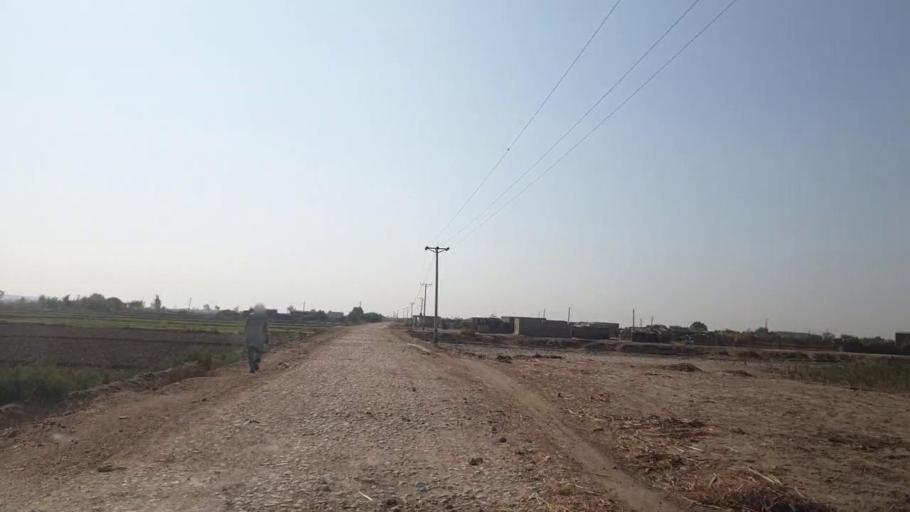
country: PK
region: Sindh
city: Thatta
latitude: 24.7332
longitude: 67.7942
